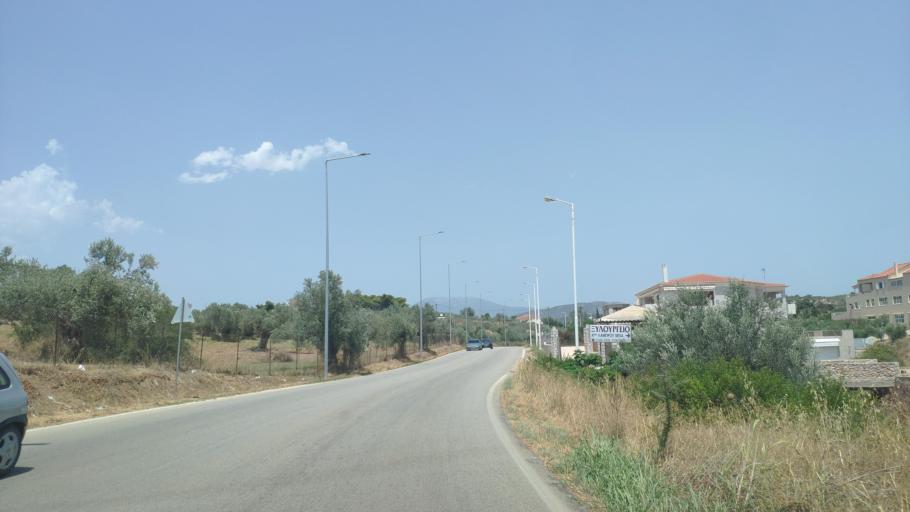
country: GR
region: Peloponnese
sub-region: Nomos Argolidos
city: Kranidi
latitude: 37.3579
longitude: 23.1605
